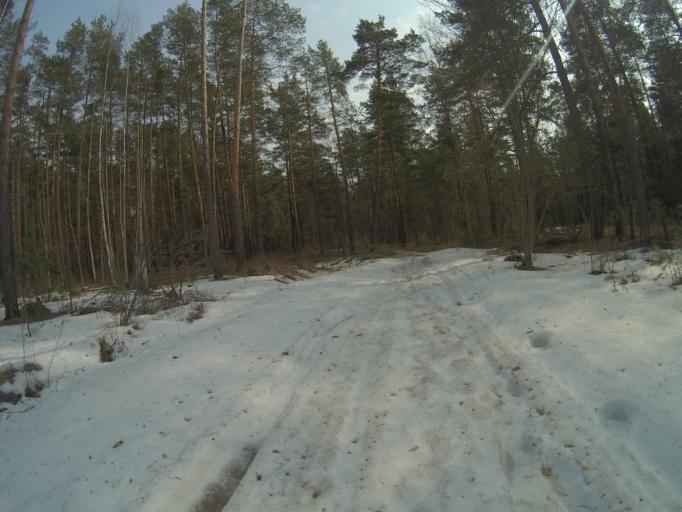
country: RU
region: Vladimir
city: Raduzhnyy
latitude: 56.0324
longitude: 40.3757
